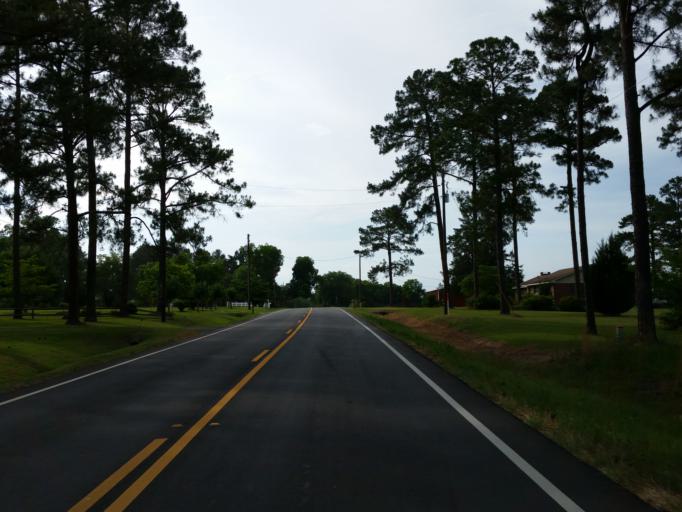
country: US
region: Georgia
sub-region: Turner County
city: Ashburn
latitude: 31.7718
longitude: -83.6900
